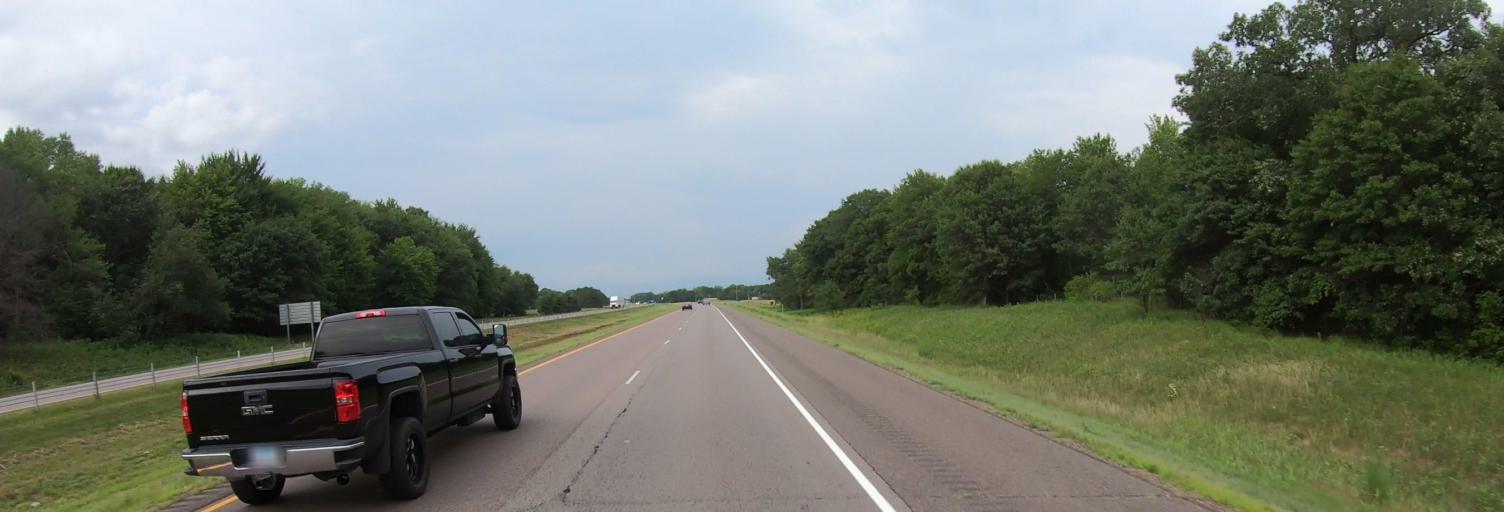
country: US
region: Minnesota
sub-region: Chisago County
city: Stacy
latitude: 45.4367
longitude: -92.9893
